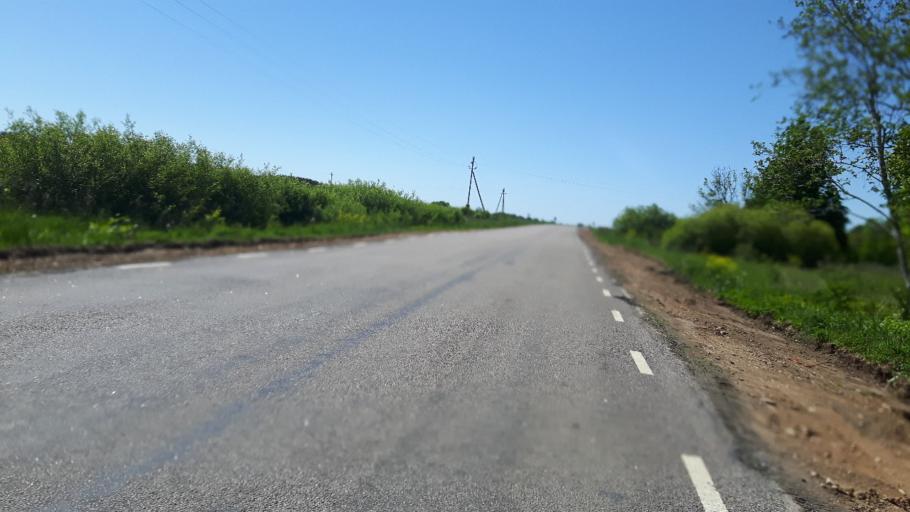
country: EE
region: Ida-Virumaa
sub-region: Narva-Joesuu linn
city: Narva-Joesuu
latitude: 59.4036
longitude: 27.9383
